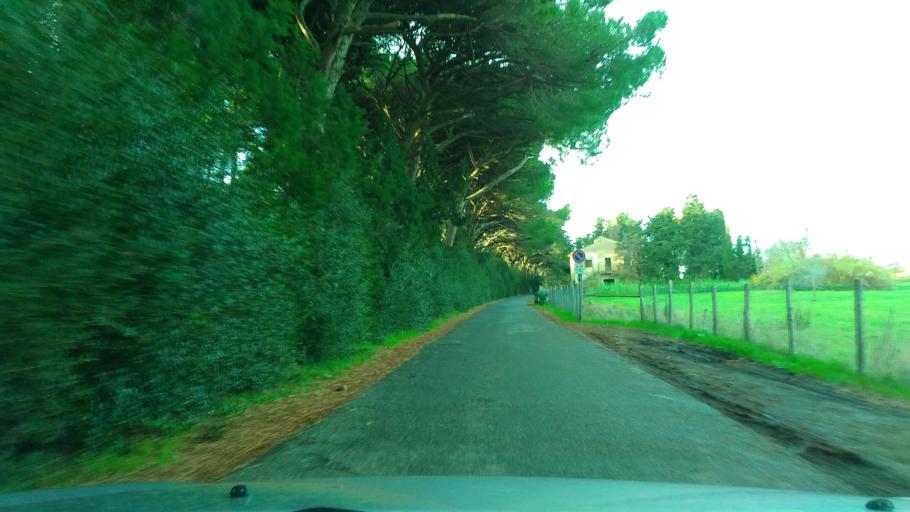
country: IT
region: Tuscany
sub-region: Provincia di Livorno
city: Cecina
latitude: 43.2813
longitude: 10.5134
